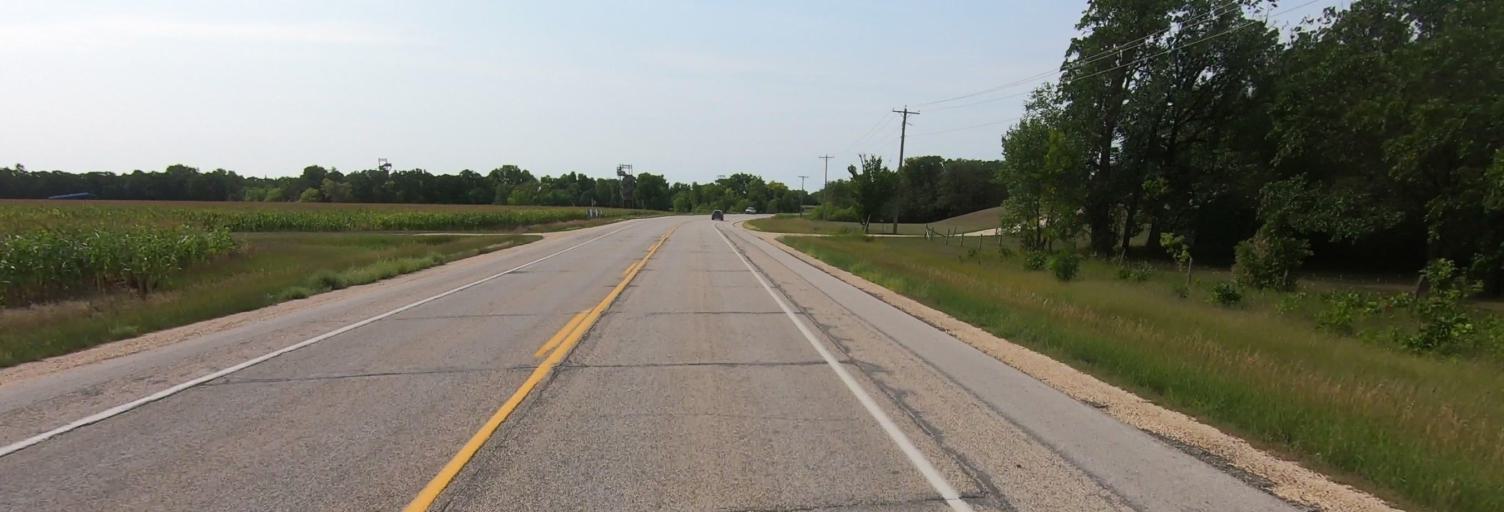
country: CA
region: Manitoba
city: Niverville
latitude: 49.7022
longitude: -97.0929
